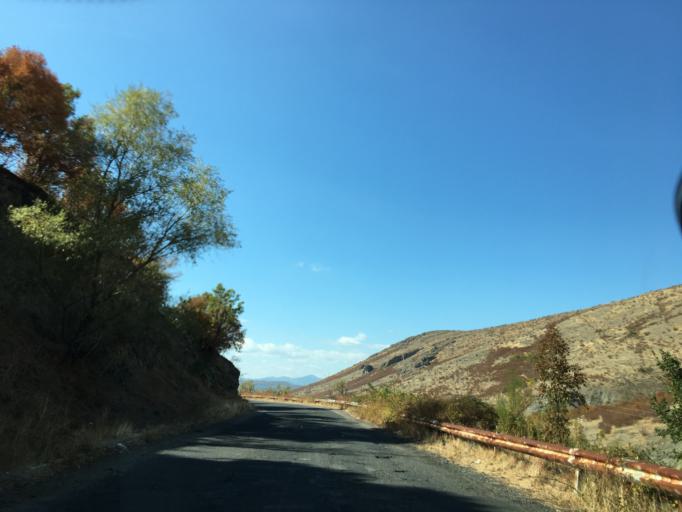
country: BG
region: Kurdzhali
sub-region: Obshtina Kurdzhali
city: Kurdzhali
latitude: 41.5253
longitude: 25.4454
